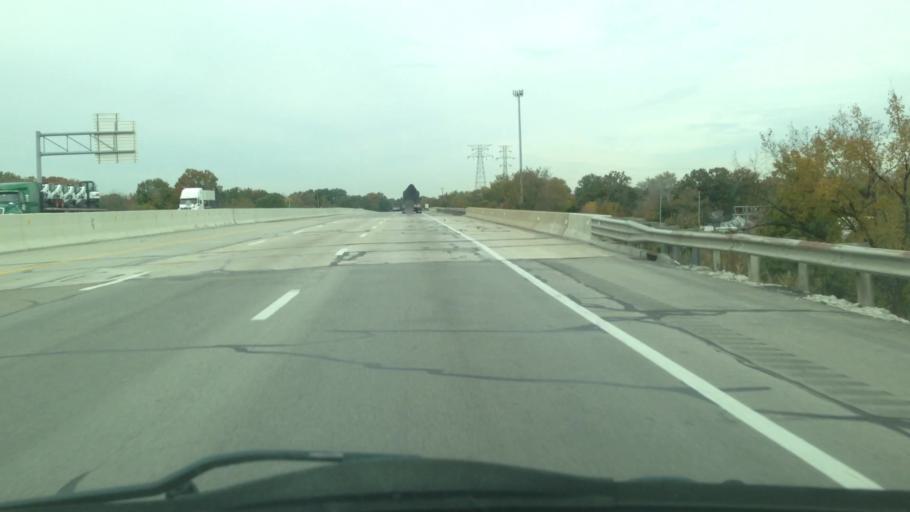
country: US
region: Ohio
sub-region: Wood County
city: Perrysburg
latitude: 41.5755
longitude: -83.5959
